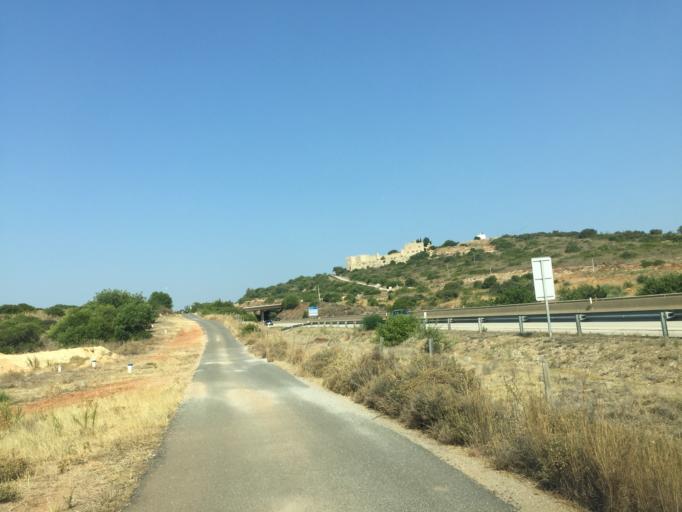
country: PT
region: Faro
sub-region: Loule
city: Almancil
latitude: 37.0987
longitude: -8.0048
